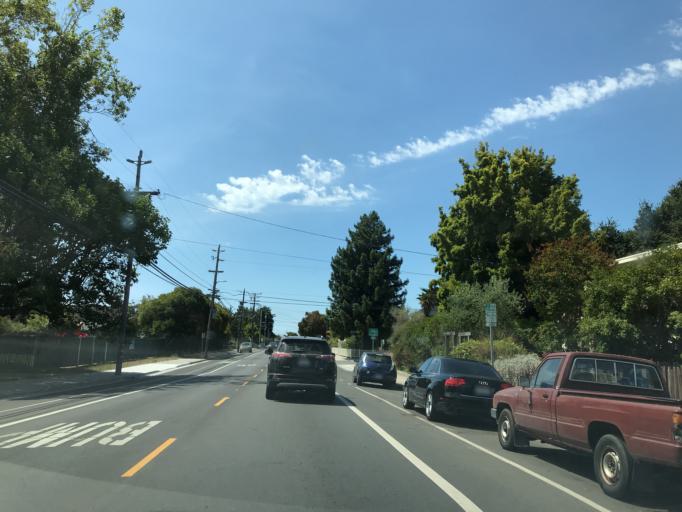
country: US
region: California
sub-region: Santa Cruz County
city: Santa Cruz
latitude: 36.9667
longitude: -122.0351
